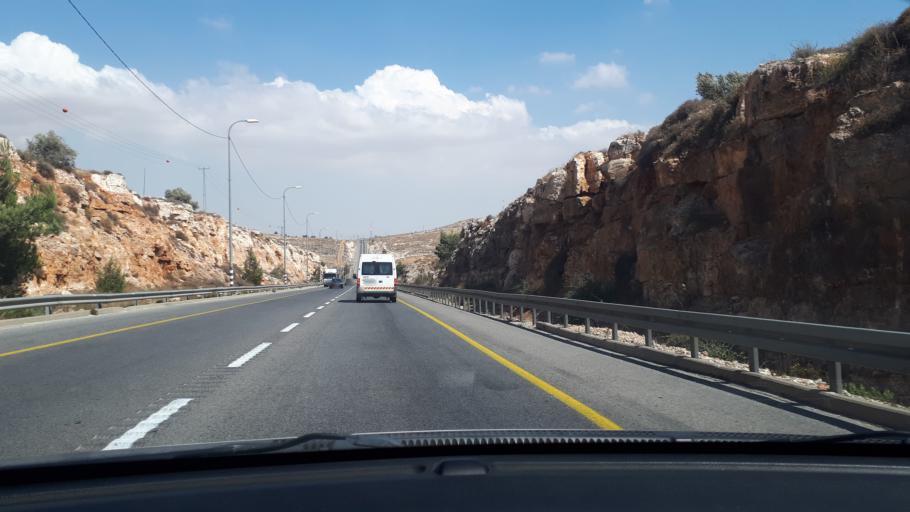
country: PS
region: West Bank
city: Burqah
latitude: 31.9004
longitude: 35.2624
